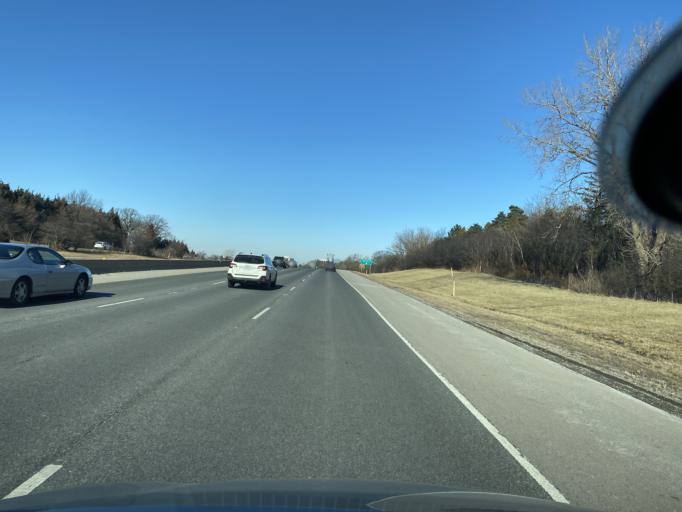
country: US
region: Illinois
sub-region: DuPage County
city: Oak Brook
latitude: 41.8257
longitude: -87.9533
